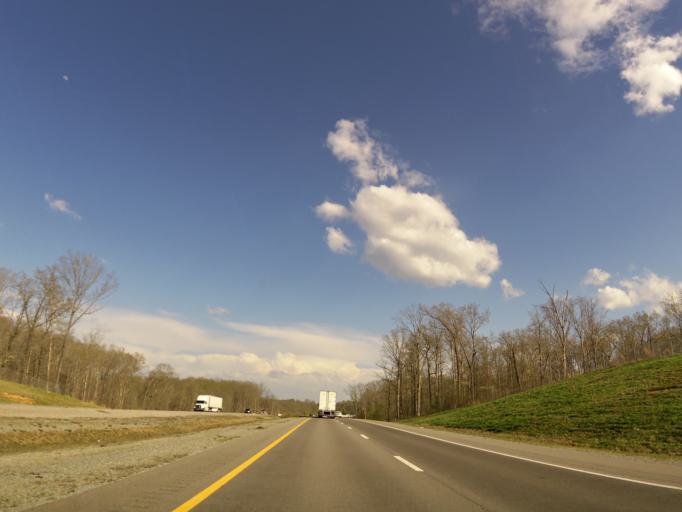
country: US
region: Tennessee
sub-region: Williamson County
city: Fairview
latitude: 35.8568
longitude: -87.0779
